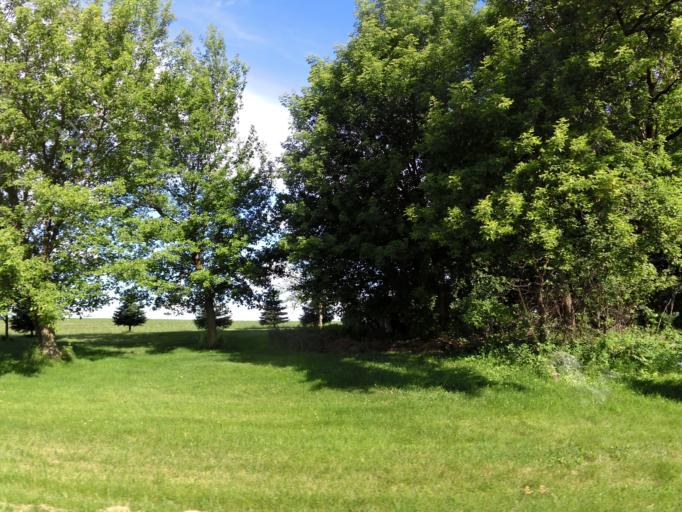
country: US
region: Minnesota
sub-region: Goodhue County
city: Cannon Falls
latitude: 44.6217
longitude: -92.9671
